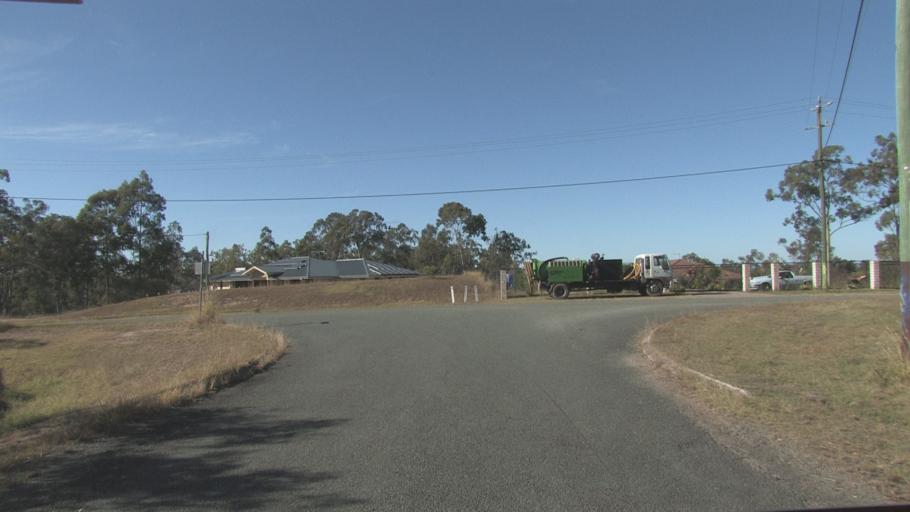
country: AU
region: Queensland
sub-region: Ipswich
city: Springfield Lakes
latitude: -27.7037
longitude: 152.9272
